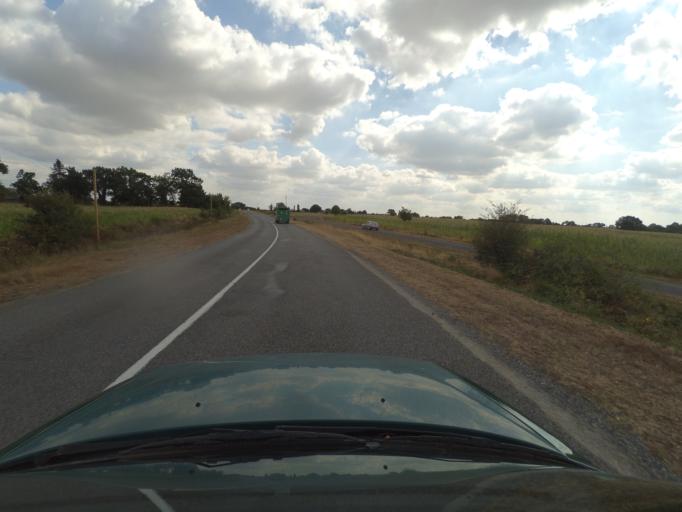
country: FR
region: Pays de la Loire
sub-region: Departement de la Loire-Atlantique
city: Aigrefeuille-sur-Maine
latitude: 47.0481
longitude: -1.4158
